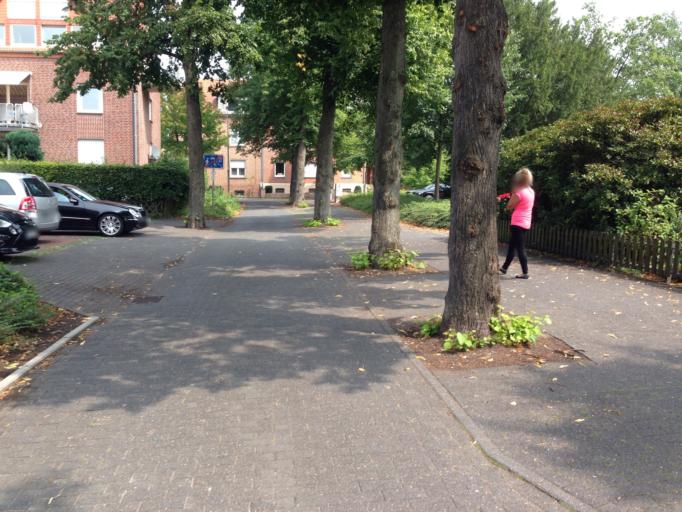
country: DE
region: North Rhine-Westphalia
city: Ludinghausen
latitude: 51.7665
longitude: 7.4392
